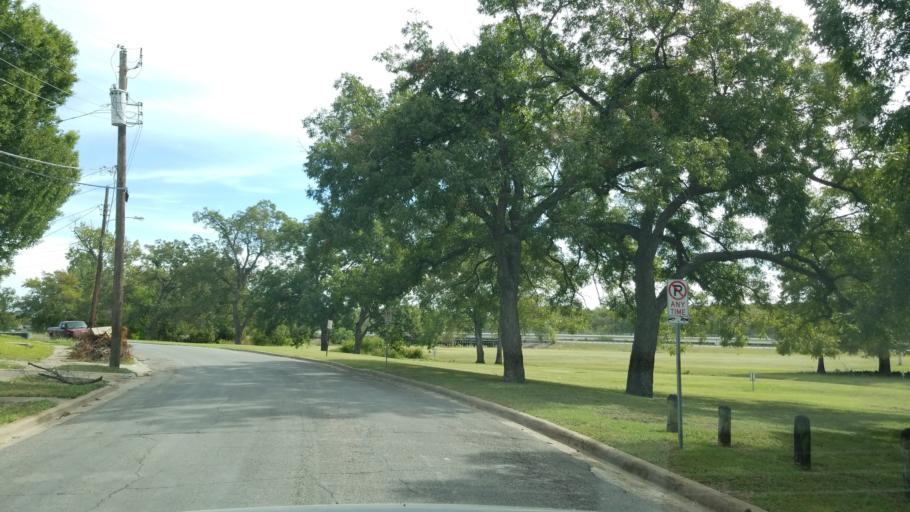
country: US
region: Texas
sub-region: Dallas County
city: Dallas
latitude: 32.7687
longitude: -96.7253
